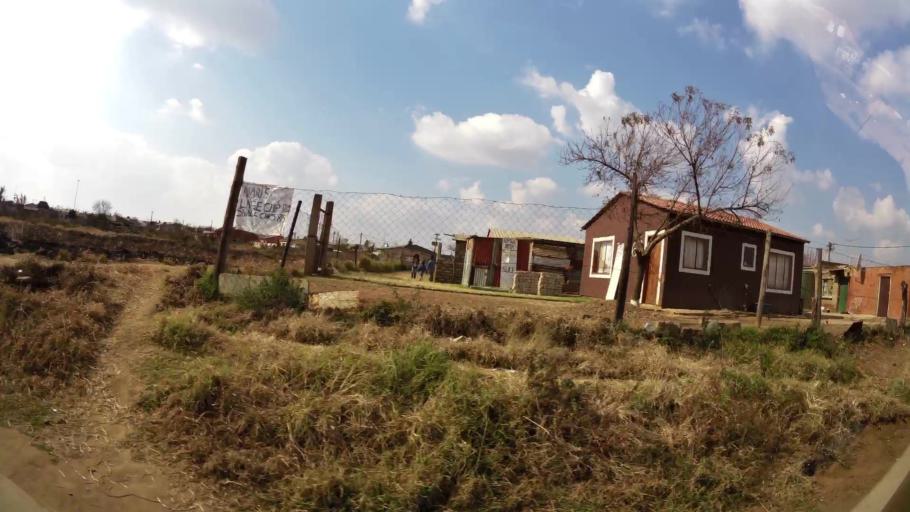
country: ZA
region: Gauteng
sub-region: Ekurhuleni Metropolitan Municipality
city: Springs
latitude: -26.1282
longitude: 28.4764
